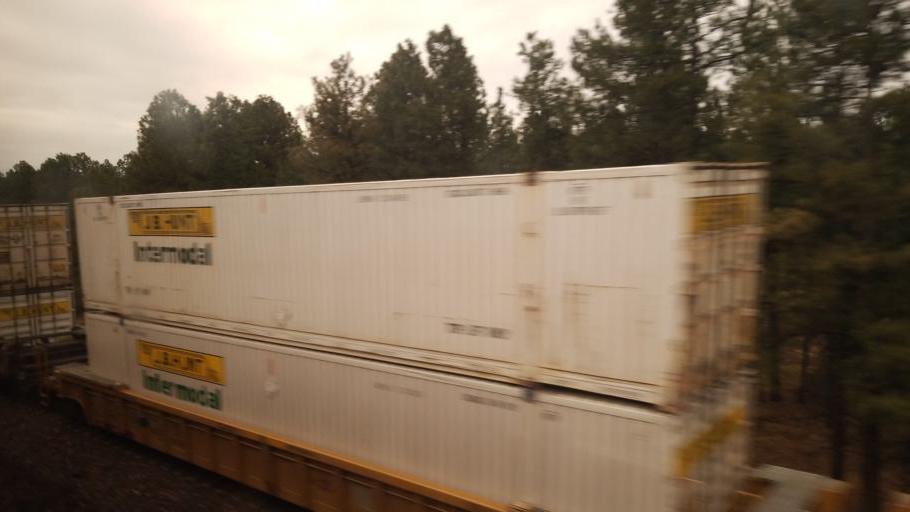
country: US
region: Arizona
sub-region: Coconino County
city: Parks
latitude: 35.2496
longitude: -111.9590
